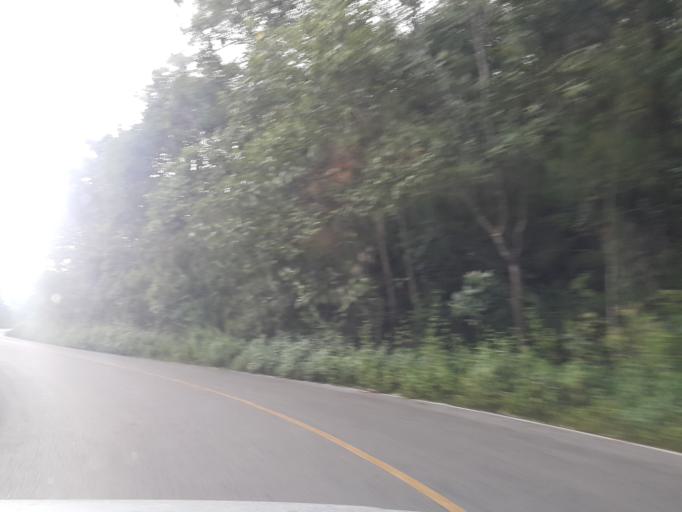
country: TH
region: Mae Hong Son
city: Khun Yuam
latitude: 18.7655
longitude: 98.1759
